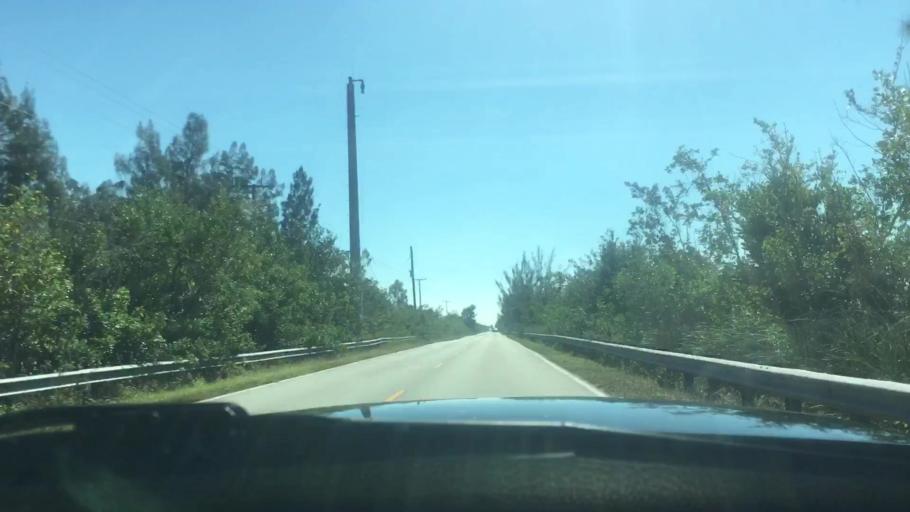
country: US
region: Florida
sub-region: Miami-Dade County
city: Florida City
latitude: 25.3644
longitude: -80.4282
